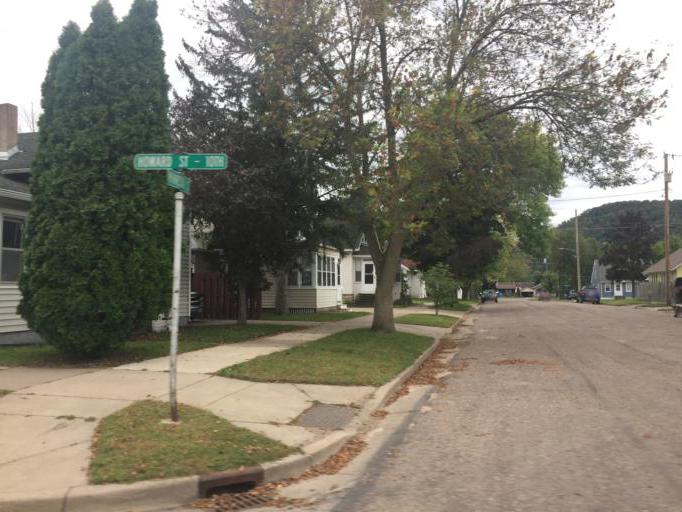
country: US
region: Minnesota
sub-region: Winona County
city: Winona
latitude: 44.0503
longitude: -91.6587
